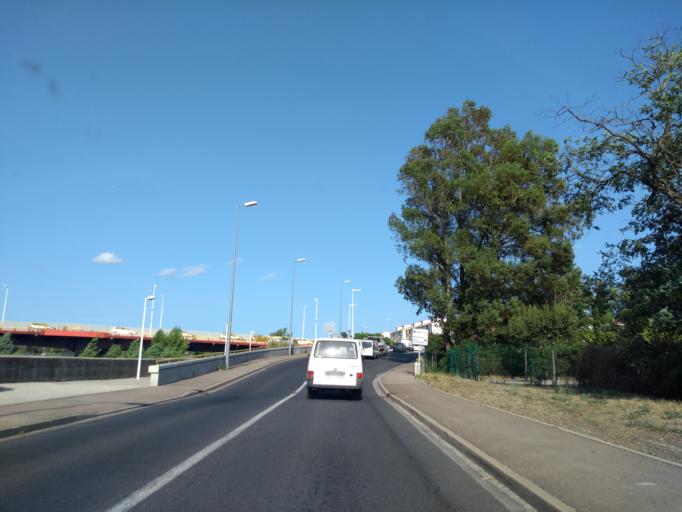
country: FR
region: Languedoc-Roussillon
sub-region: Departement des Pyrenees-Orientales
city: Perpignan
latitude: 42.7051
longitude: 2.9006
